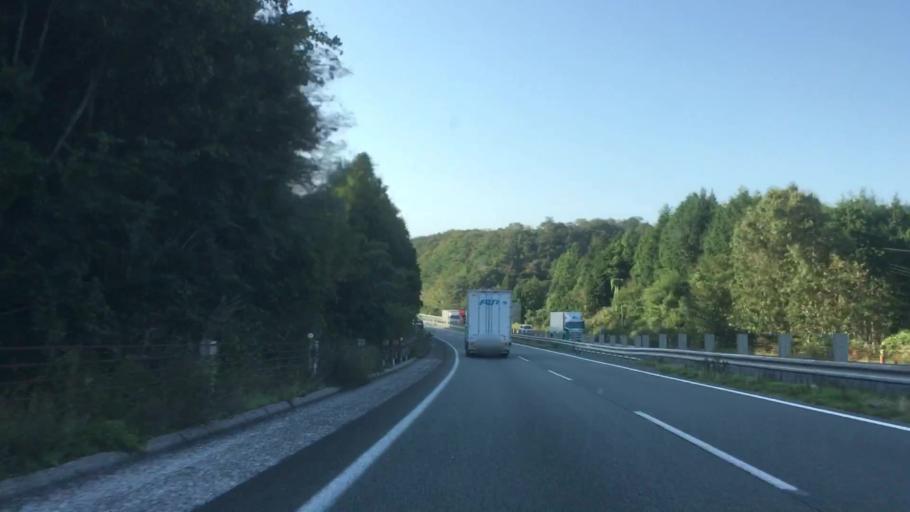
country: JP
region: Yamaguchi
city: Ogori-shimogo
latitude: 34.1591
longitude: 131.3312
